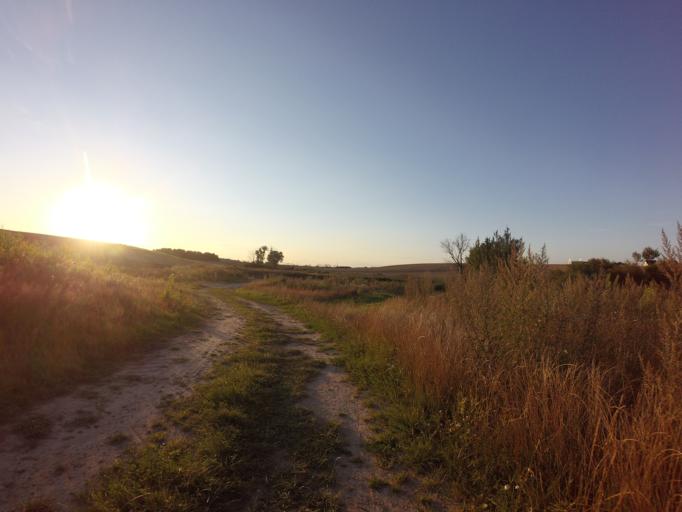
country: PL
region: West Pomeranian Voivodeship
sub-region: Powiat choszczenski
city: Choszczno
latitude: 53.1815
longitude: 15.4114
